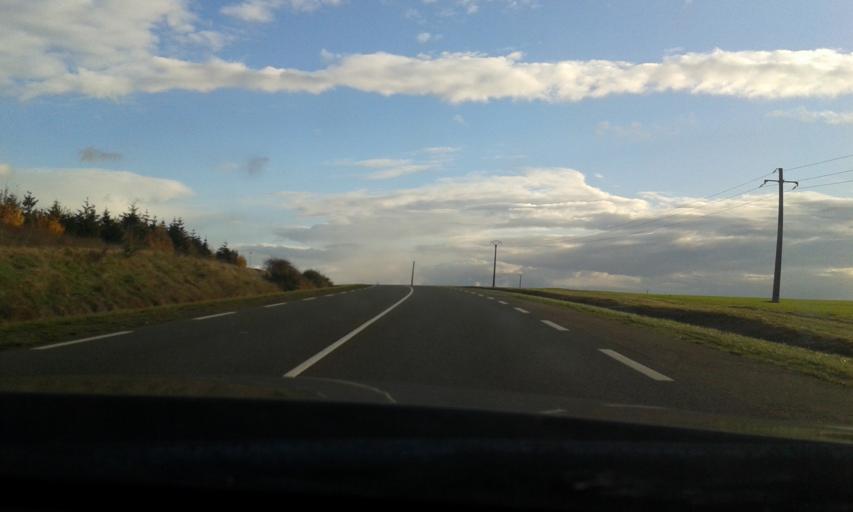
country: FR
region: Centre
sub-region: Departement d'Eure-et-Loir
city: Leves
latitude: 48.4757
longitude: 1.4612
